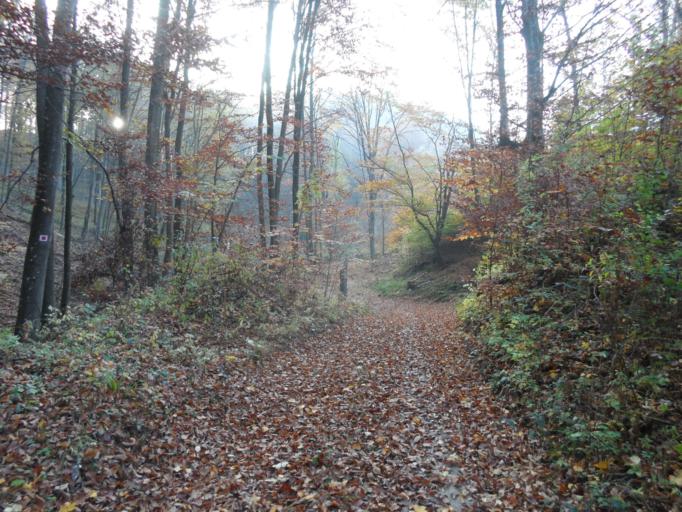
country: HU
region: Veszprem
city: Herend
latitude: 47.2295
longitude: 17.7398
